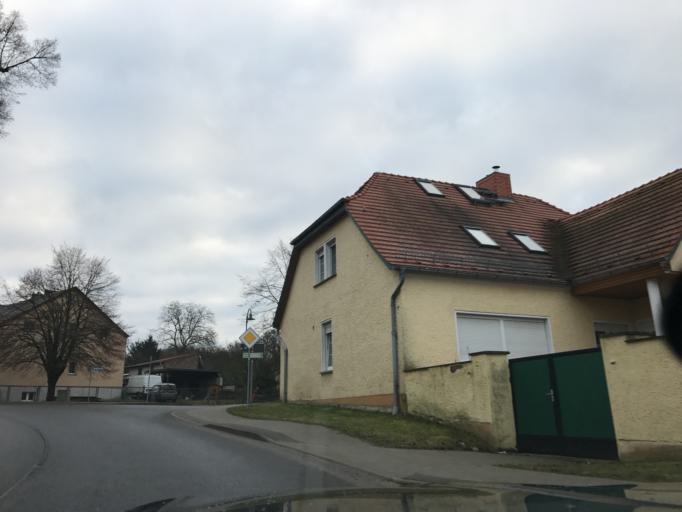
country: DE
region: Brandenburg
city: Werder
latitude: 52.3635
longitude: 12.9615
